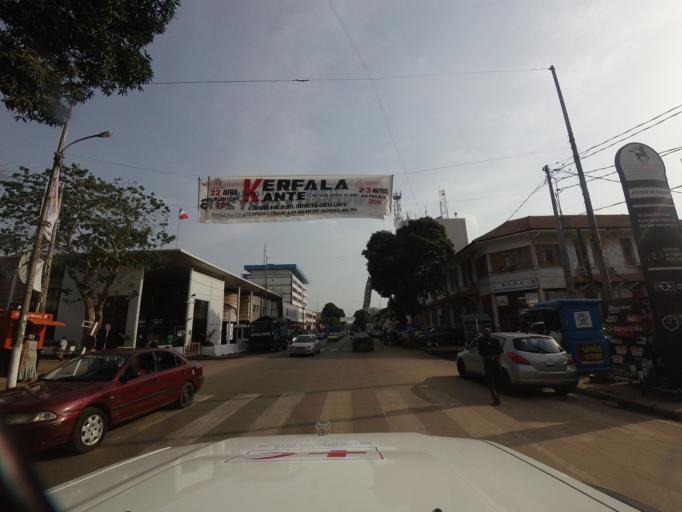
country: GN
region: Conakry
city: Camayenne
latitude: 9.5112
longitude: -13.7146
